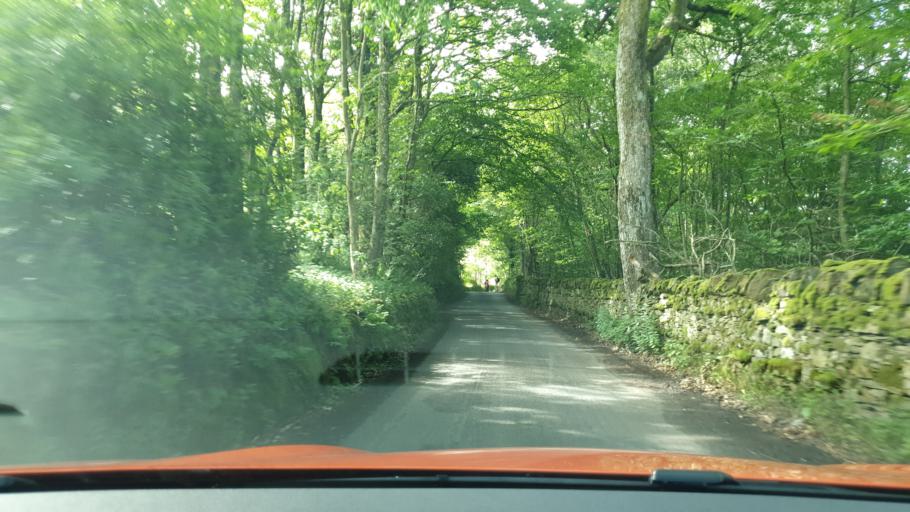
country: GB
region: England
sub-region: Cumbria
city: Penrith
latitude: 54.5800
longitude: -2.8535
